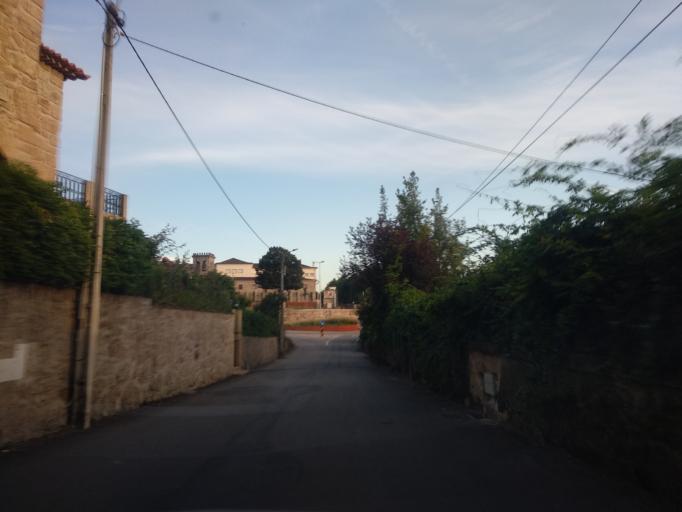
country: PT
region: Braga
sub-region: Vila Nova de Famalicao
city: Vila Nova de Famalicao
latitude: 41.4036
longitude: -8.5104
